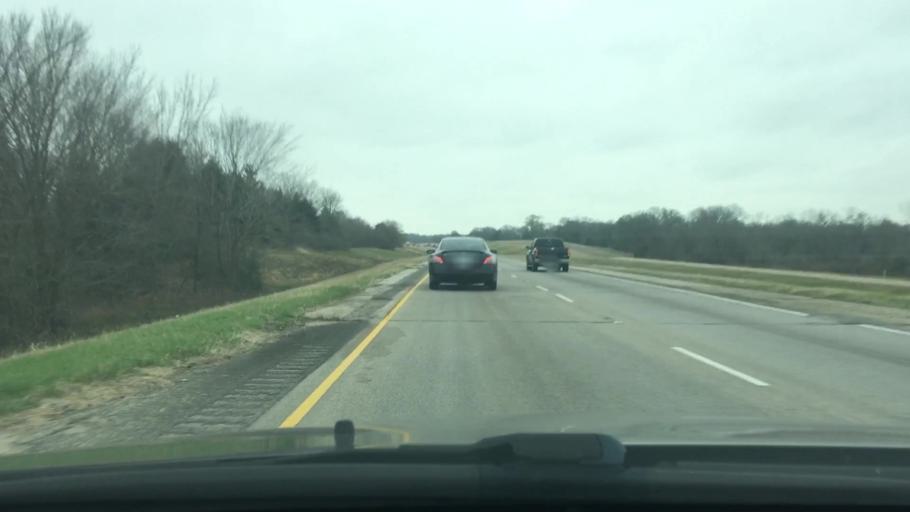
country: US
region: Texas
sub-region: Freestone County
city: Fairfield
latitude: 31.7953
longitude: -96.2531
